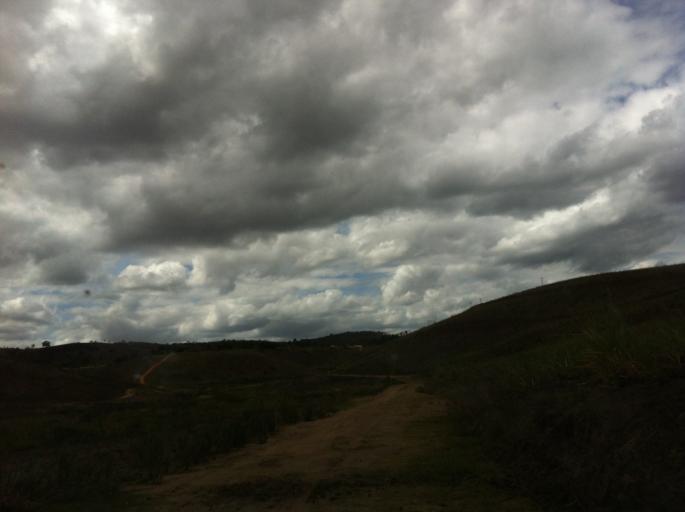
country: BR
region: Alagoas
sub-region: Ibateguara
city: Ibateguara
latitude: -8.9591
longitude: -35.9511
